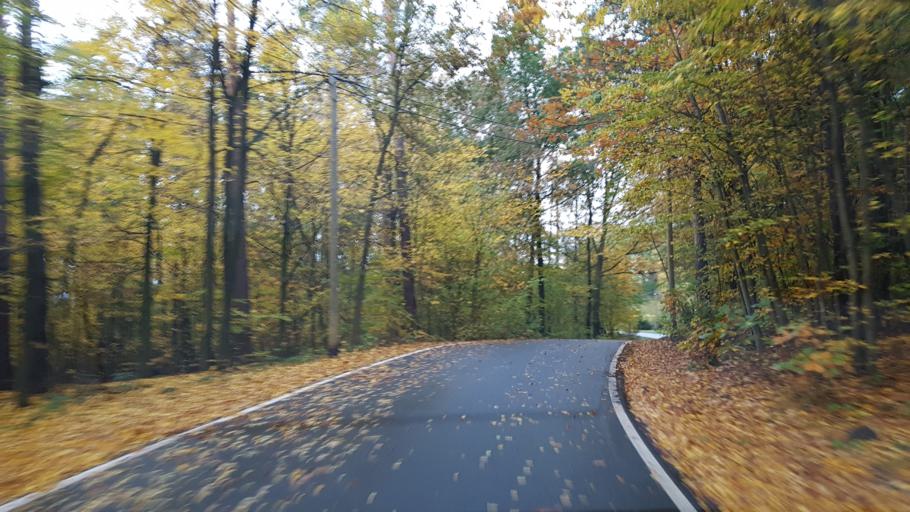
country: DE
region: Saxony
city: Cavertitz
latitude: 51.3941
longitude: 13.0638
